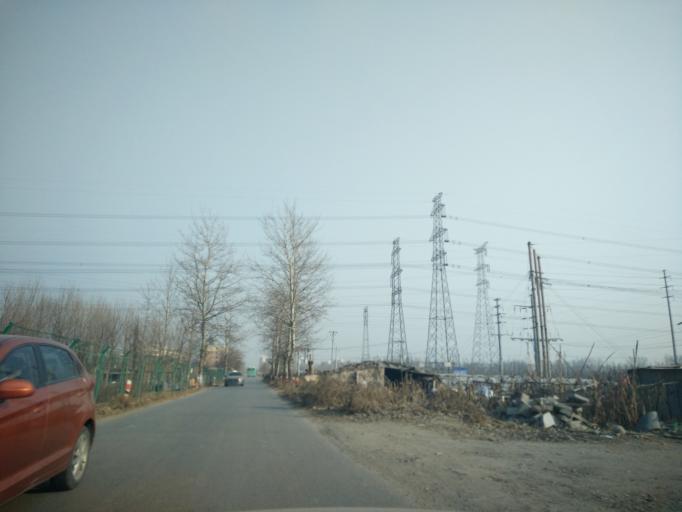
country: CN
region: Beijing
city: Xingfeng
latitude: 39.7169
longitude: 116.3807
